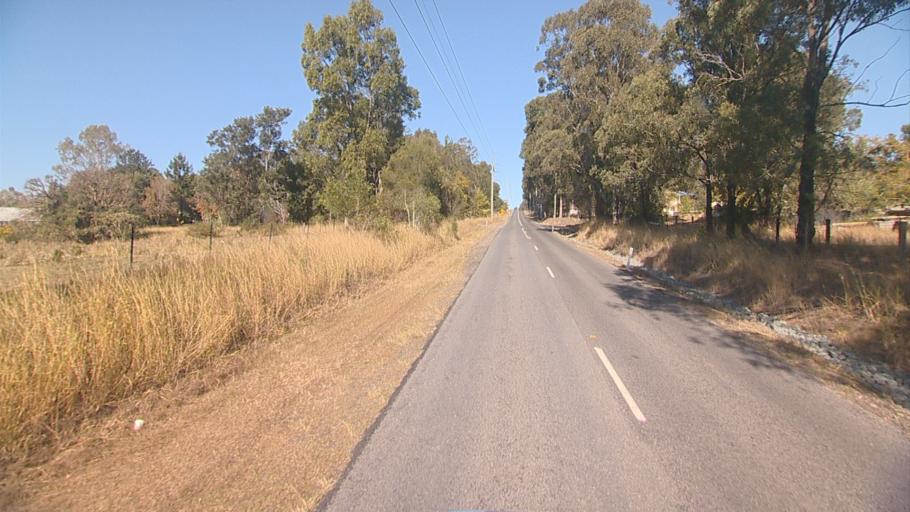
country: AU
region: Queensland
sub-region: Logan
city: Cedar Vale
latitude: -27.8741
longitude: 153.0169
